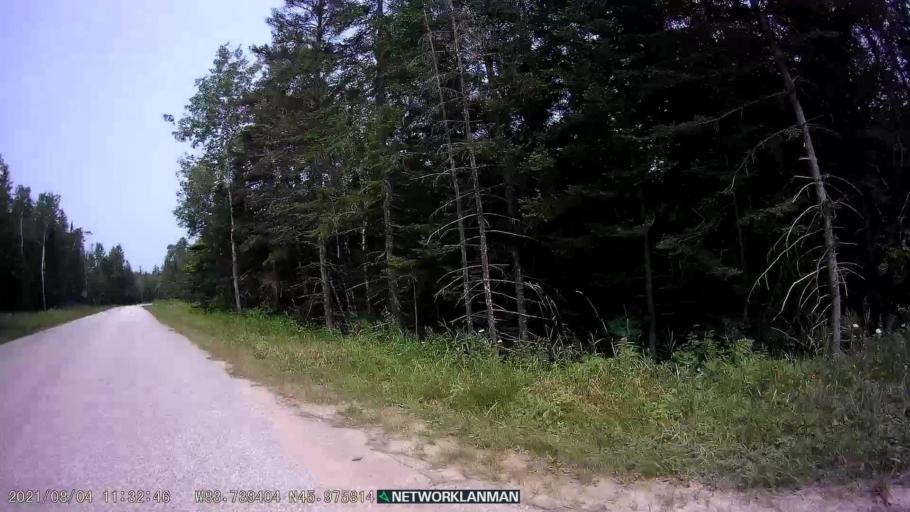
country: CA
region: Ontario
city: Thessalon
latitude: 45.9760
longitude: -83.7392
